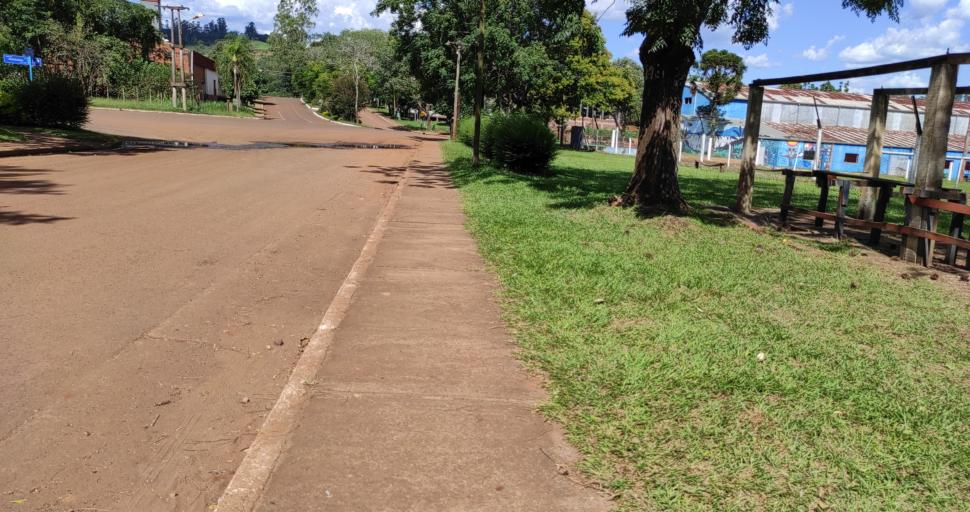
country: AR
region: Misiones
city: El Soberbio
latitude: -27.2979
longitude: -54.1966
